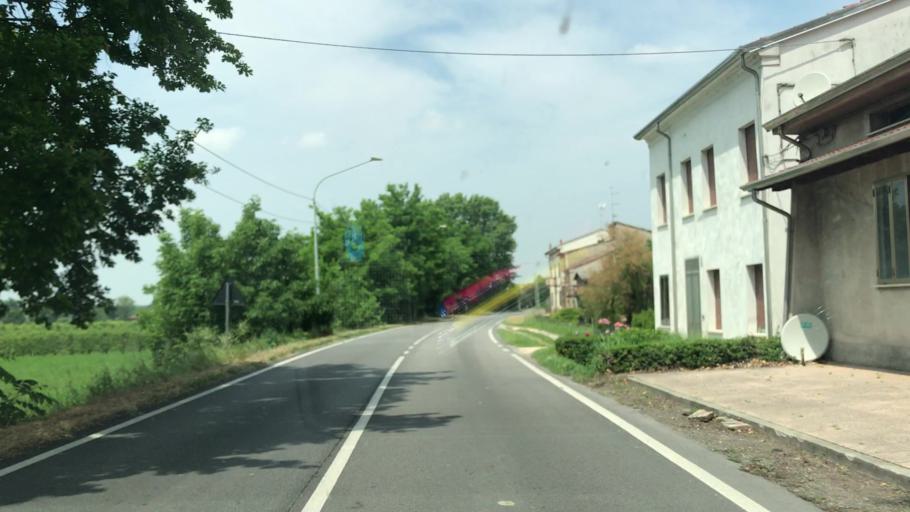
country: IT
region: Lombardy
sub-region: Provincia di Mantova
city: Borgofranco sul Po
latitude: 45.0404
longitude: 11.2178
